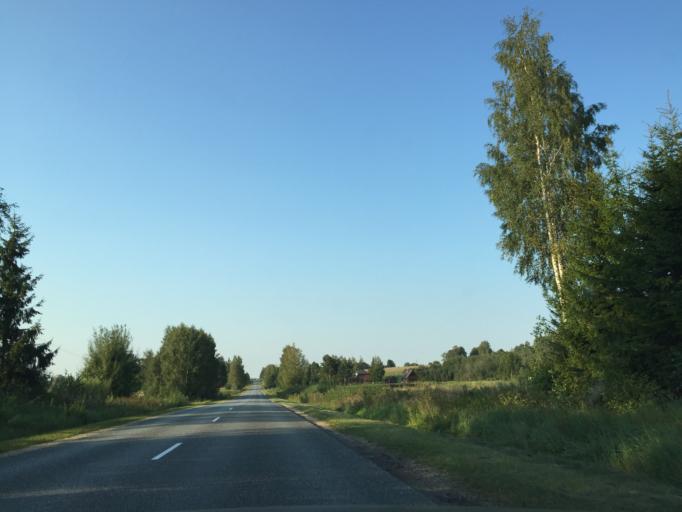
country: LV
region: Limbazu Rajons
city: Limbazi
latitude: 57.5629
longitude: 24.7663
